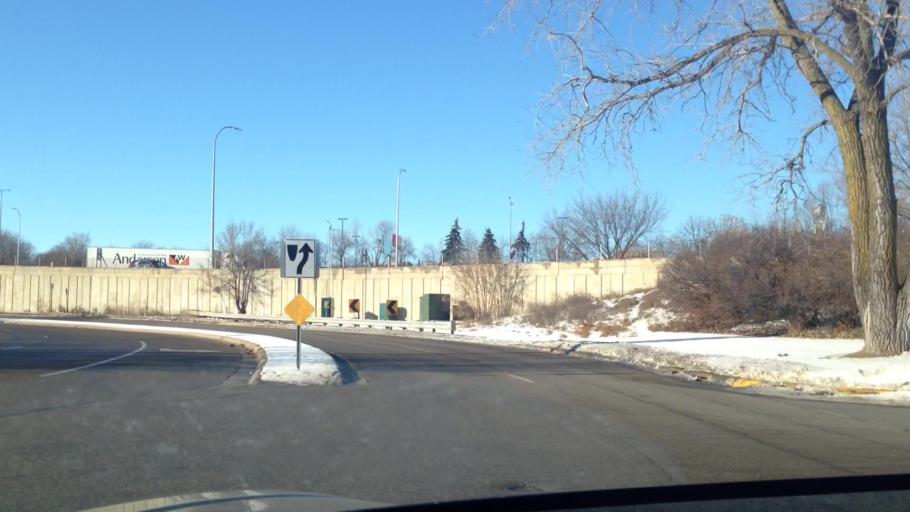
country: US
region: Minnesota
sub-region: Hennepin County
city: Saint Louis Park
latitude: 44.9359
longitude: -93.3483
